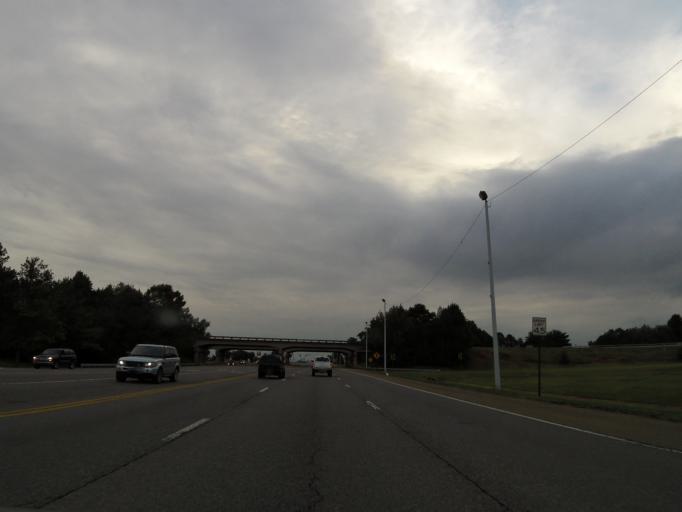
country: US
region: Alabama
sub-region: Madison County
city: Redstone Arsenal
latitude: 34.7425
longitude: -86.6720
